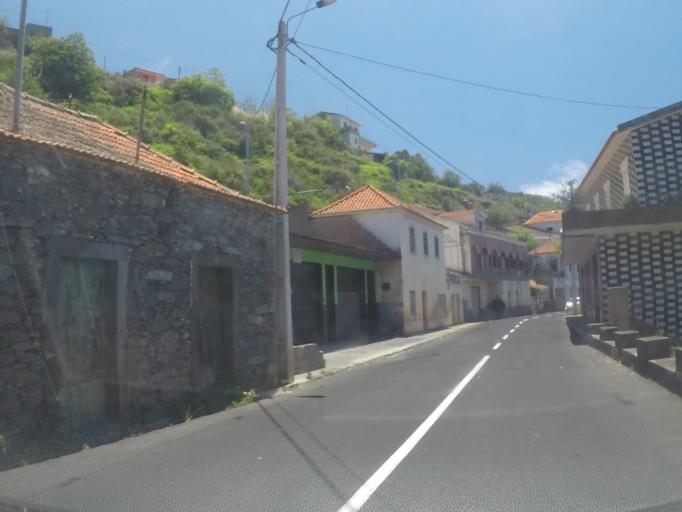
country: PT
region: Madeira
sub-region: Camara de Lobos
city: Curral das Freiras
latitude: 32.6882
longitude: -16.9937
